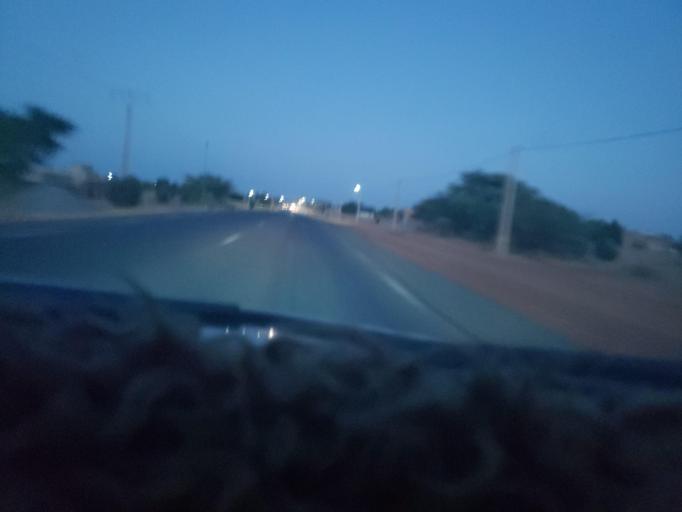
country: SN
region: Louga
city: Ndibene Dahra
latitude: 15.3817
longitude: -15.2439
